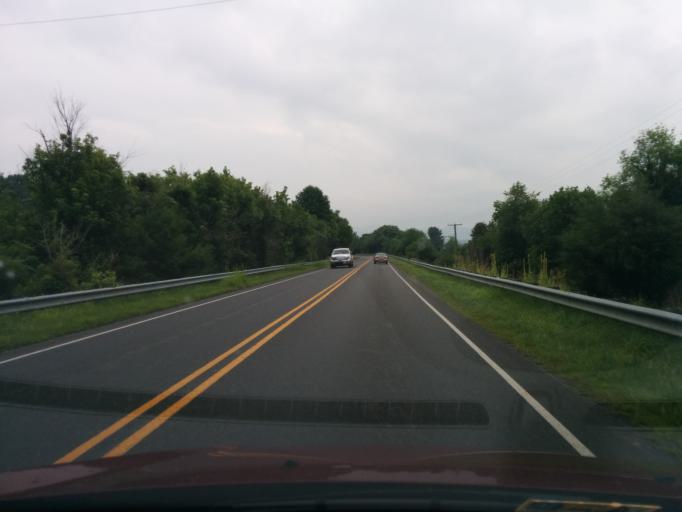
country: US
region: Virginia
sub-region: Rockbridge County
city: East Lexington
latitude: 37.8044
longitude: -79.4200
